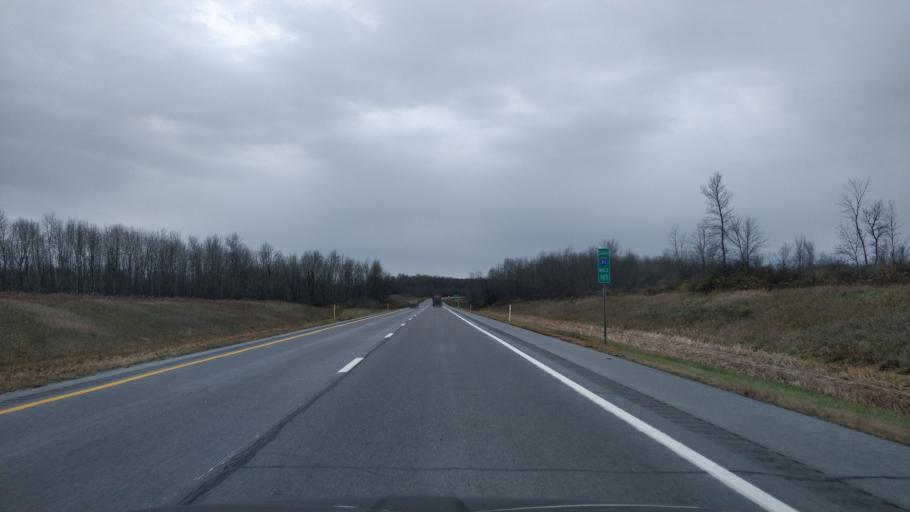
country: US
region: New York
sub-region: Jefferson County
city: Calcium
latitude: 44.1287
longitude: -75.8832
